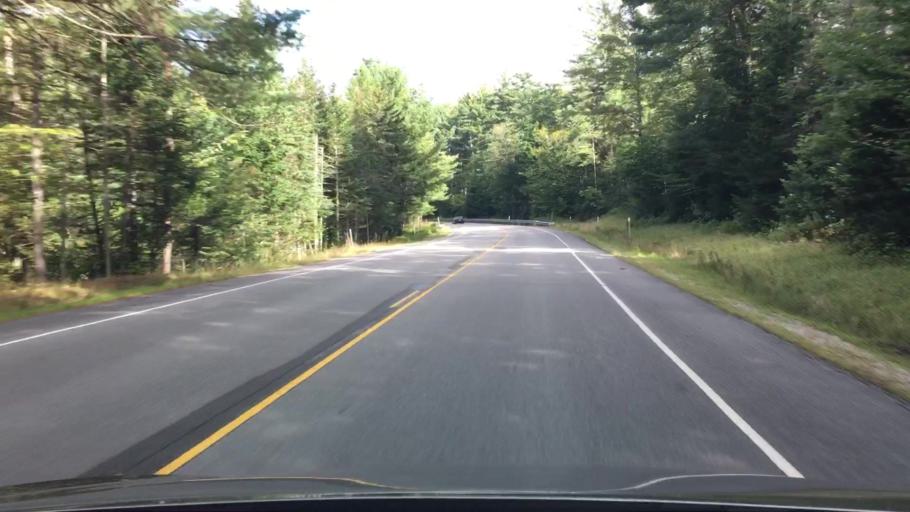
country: US
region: New Hampshire
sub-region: Carroll County
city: Tamworth
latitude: 43.9893
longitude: -71.3172
